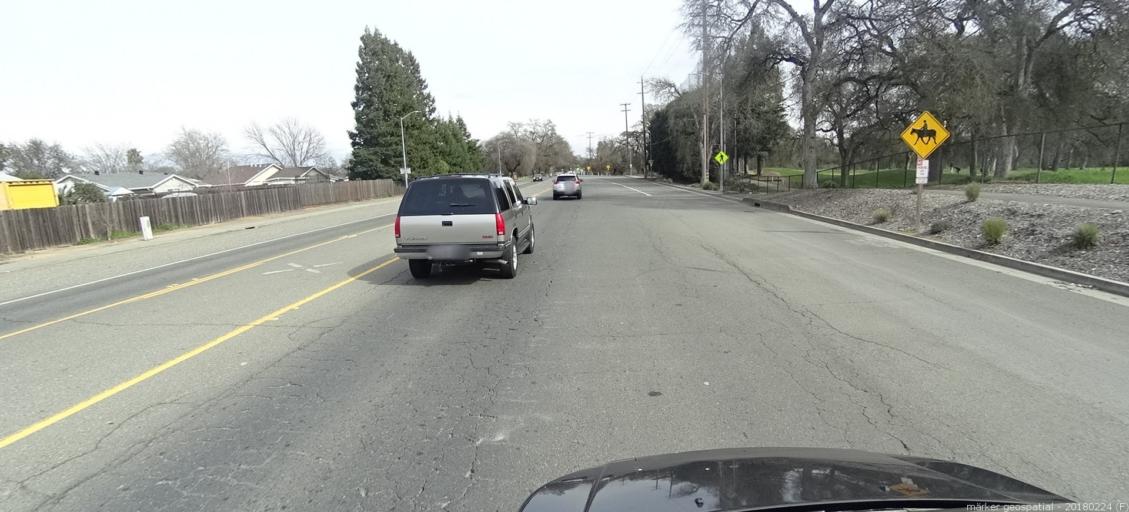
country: US
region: California
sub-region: Sacramento County
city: North Highlands
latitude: 38.7143
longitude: -121.4067
